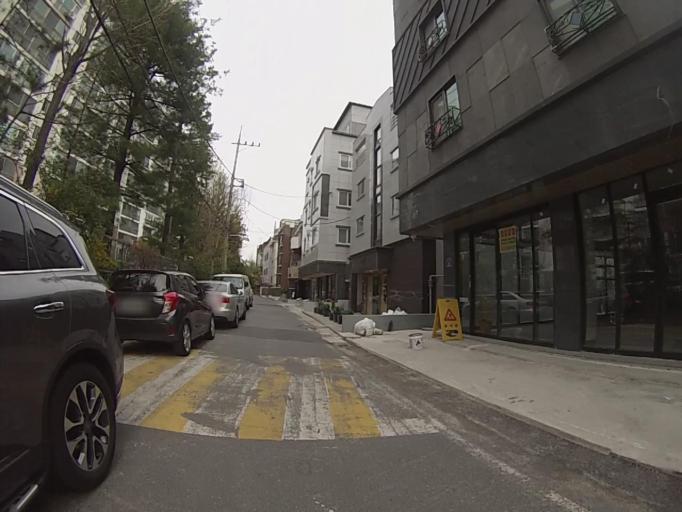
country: KR
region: Daejeon
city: Songgang-dong
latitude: 36.3623
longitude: 127.3535
